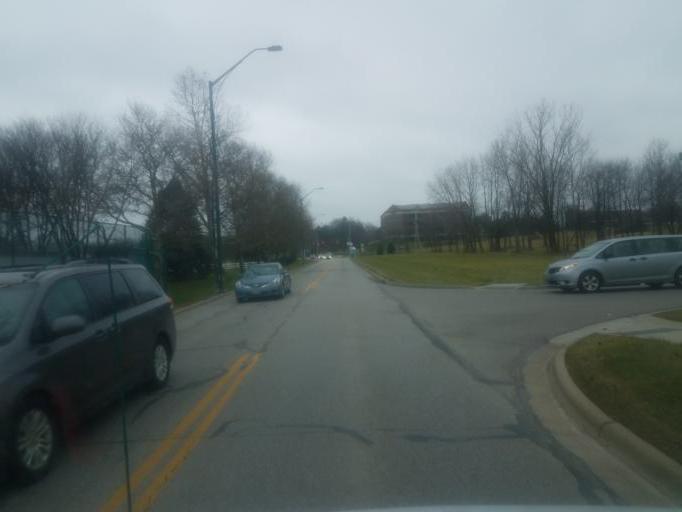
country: US
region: Ohio
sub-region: Franklin County
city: Westerville
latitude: 40.1126
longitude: -82.9428
